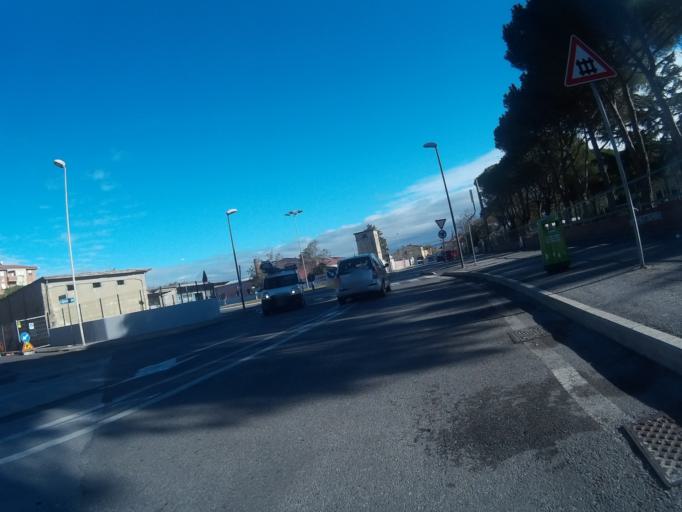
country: IT
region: Tuscany
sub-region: Provincia di Livorno
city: Livorno
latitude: 43.5612
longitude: 10.3355
